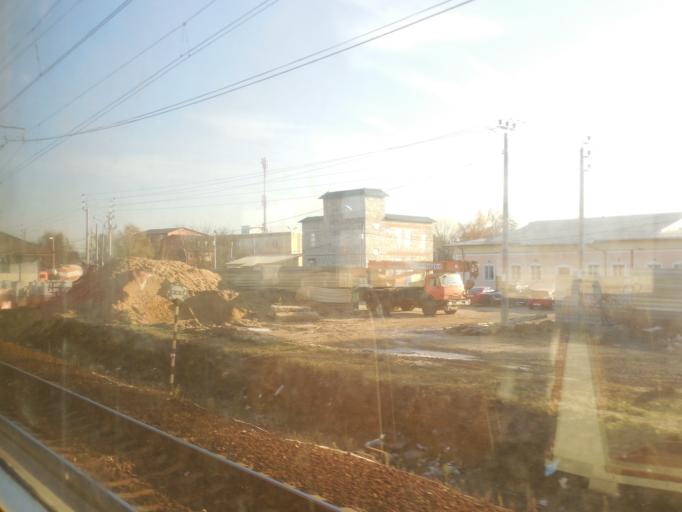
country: RU
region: Moskovskaya
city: Saltykovka
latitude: 55.7580
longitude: 37.9208
